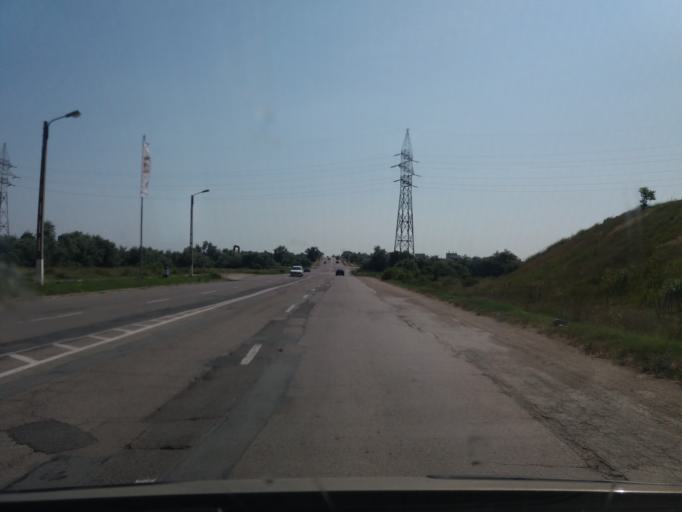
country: RO
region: Constanta
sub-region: Comuna Navodari
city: Navodari
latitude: 44.3276
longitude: 28.6266
